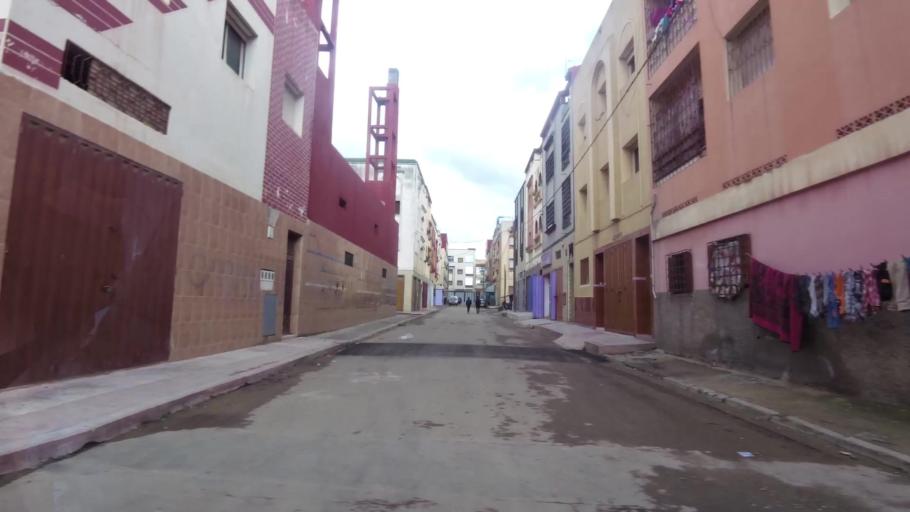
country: MA
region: Chaouia-Ouardigha
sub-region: Settat Province
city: Berrechid
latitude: 33.2664
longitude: -7.5754
